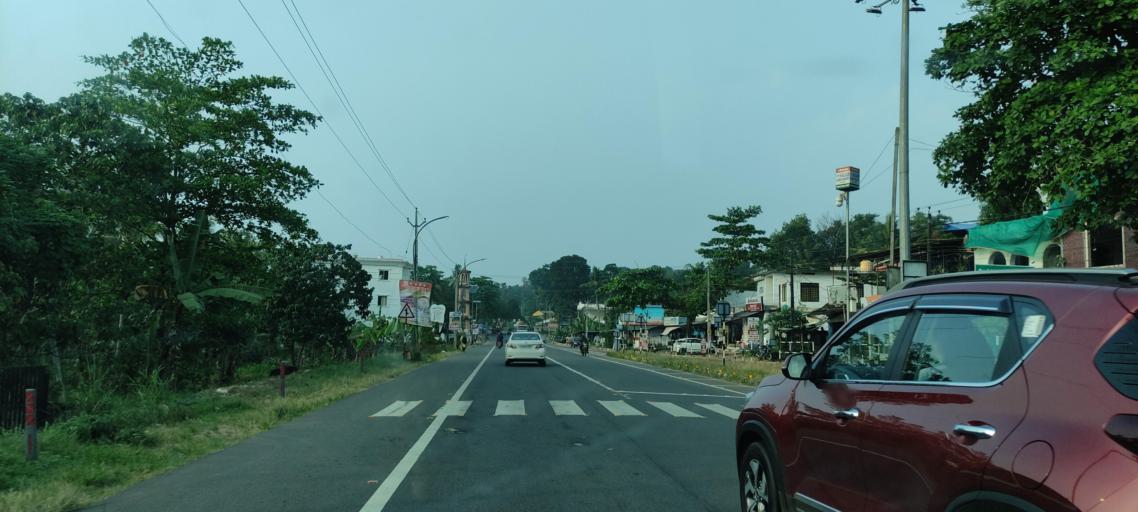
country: IN
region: Kerala
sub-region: Pattanamtitta
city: Adur
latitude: 9.0956
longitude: 76.7527
